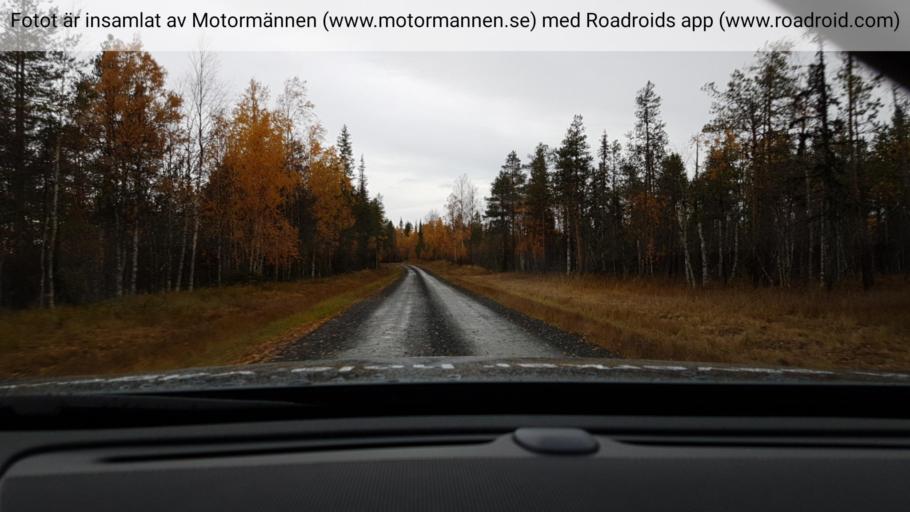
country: SE
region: Norrbotten
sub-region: Pajala Kommun
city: Pajala
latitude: 67.0956
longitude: 22.7372
